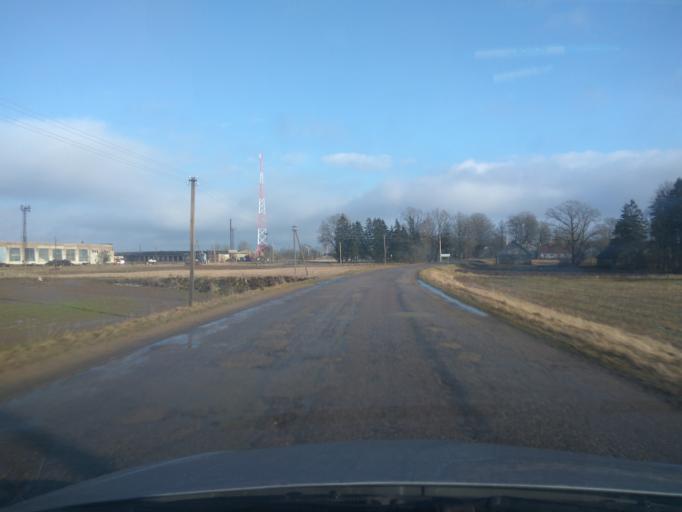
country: LV
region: Saldus Rajons
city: Saldus
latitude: 56.8272
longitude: 22.3926
